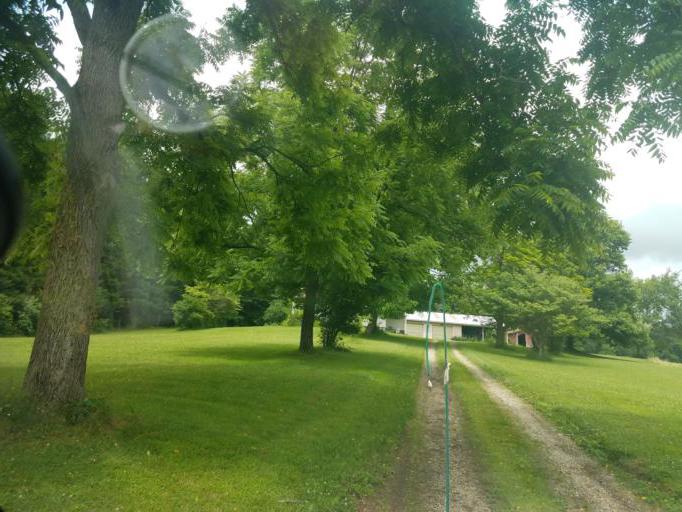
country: US
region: Ohio
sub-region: Sandusky County
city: Bellville
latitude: 40.5656
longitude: -82.4830
